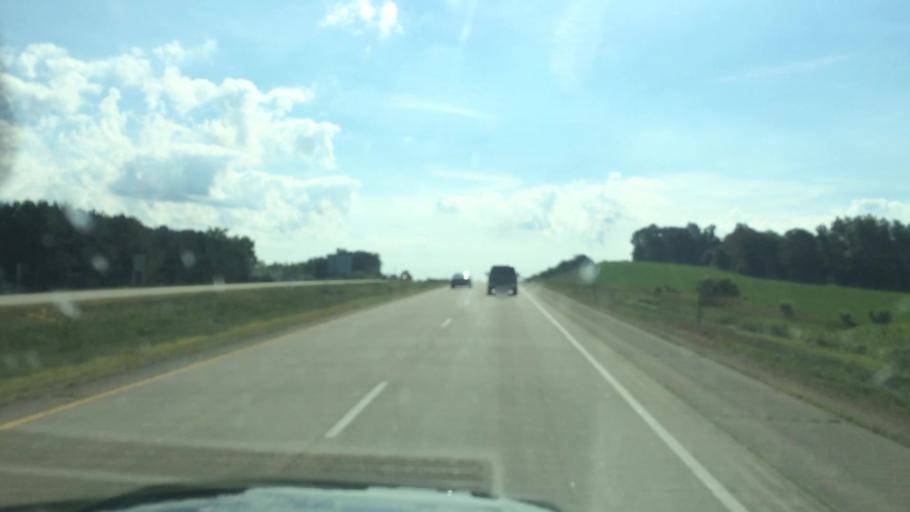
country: US
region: Wisconsin
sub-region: Shawano County
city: Wittenberg
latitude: 44.8259
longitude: -89.1096
